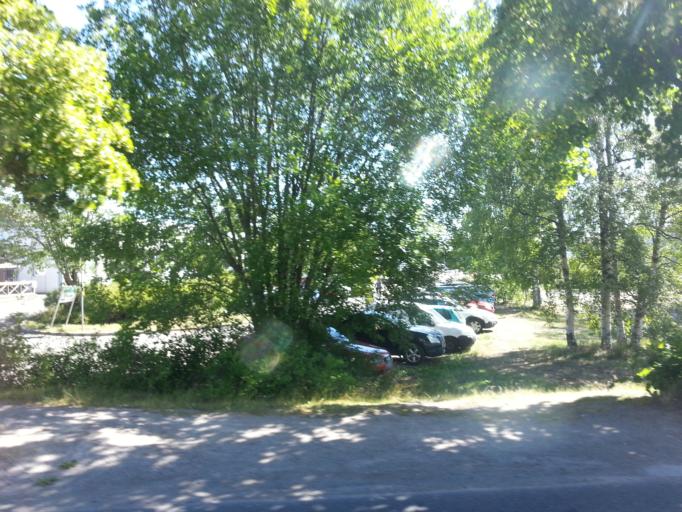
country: SE
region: Stockholm
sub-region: Tyreso Kommun
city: Bollmora
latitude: 59.2446
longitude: 18.2144
